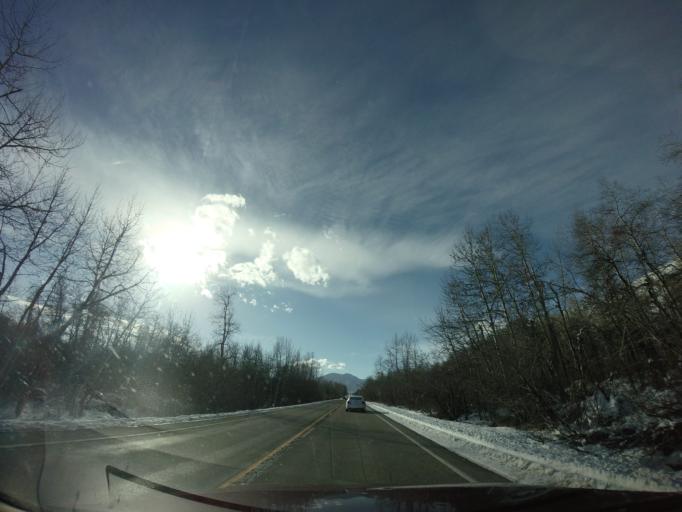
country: US
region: Montana
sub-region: Carbon County
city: Red Lodge
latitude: 45.2243
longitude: -109.2400
